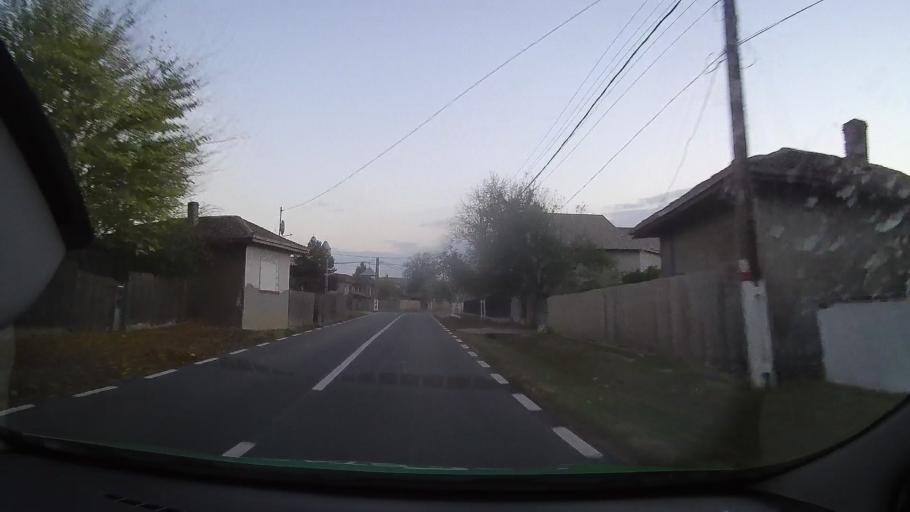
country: RO
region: Constanta
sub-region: Comuna Oltina
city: Oltina
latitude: 44.1646
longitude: 27.6672
